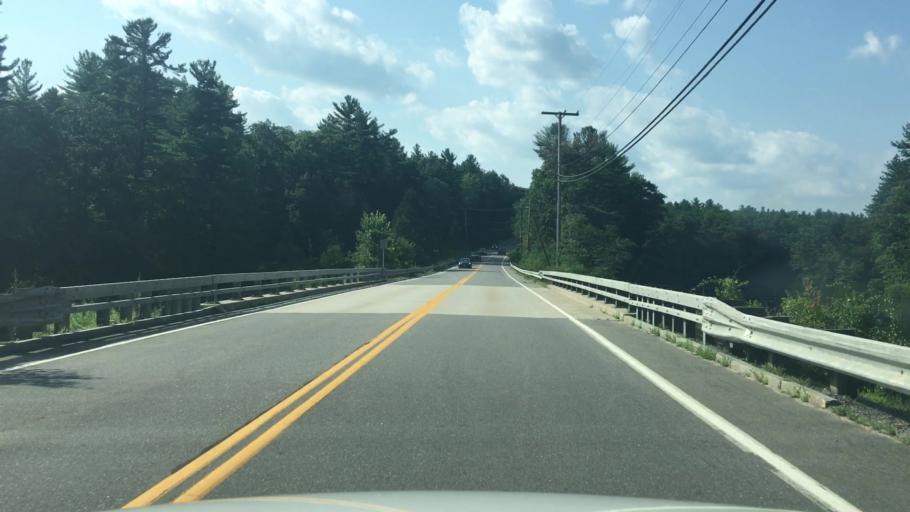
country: US
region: New Hampshire
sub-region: Rockingham County
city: Auburn
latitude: 42.9878
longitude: -71.3754
